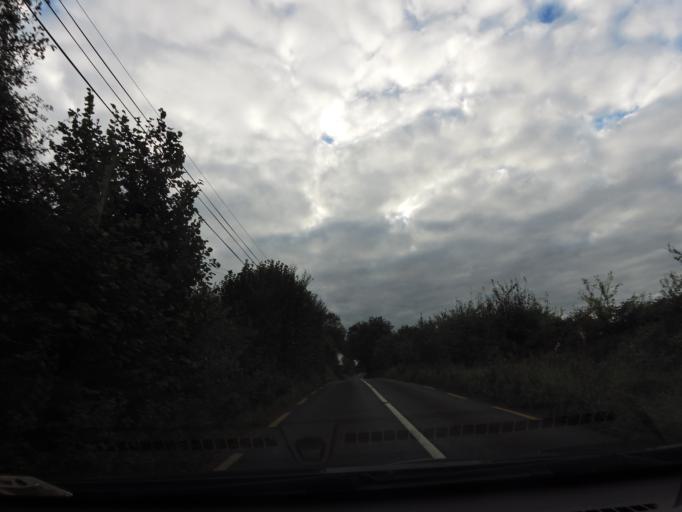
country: IE
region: Connaught
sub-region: County Galway
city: Loughrea
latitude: 53.1612
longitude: -8.5094
